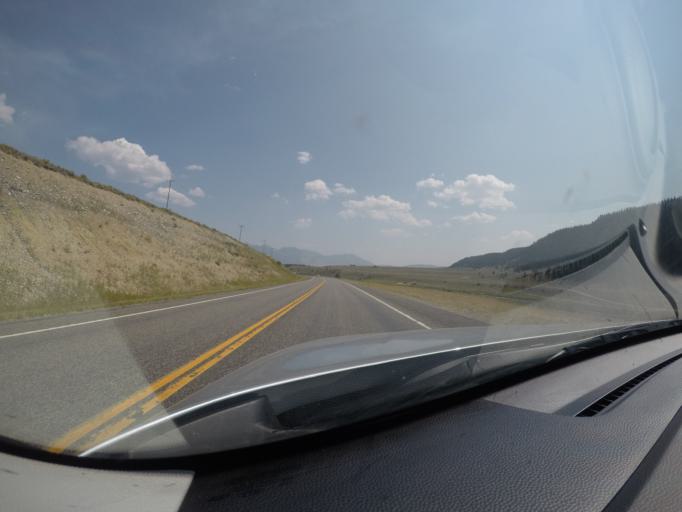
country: US
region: Montana
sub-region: Gallatin County
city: Big Sky
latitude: 44.8706
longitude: -111.5631
